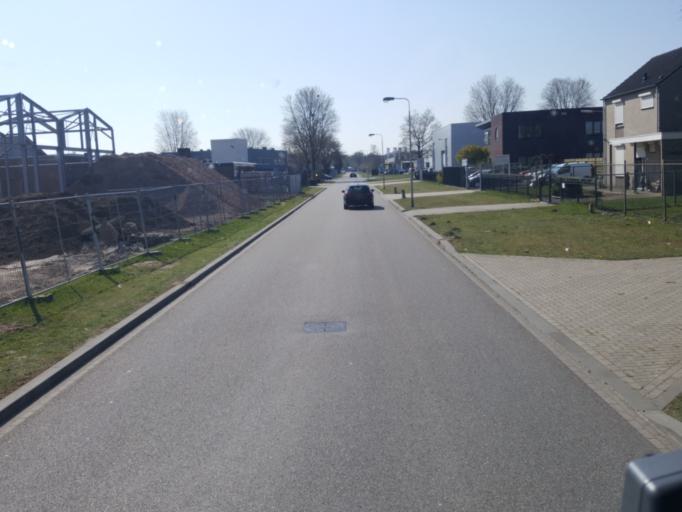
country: NL
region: North Brabant
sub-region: Gemeente Oss
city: Berghem
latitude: 51.7639
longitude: 5.5499
